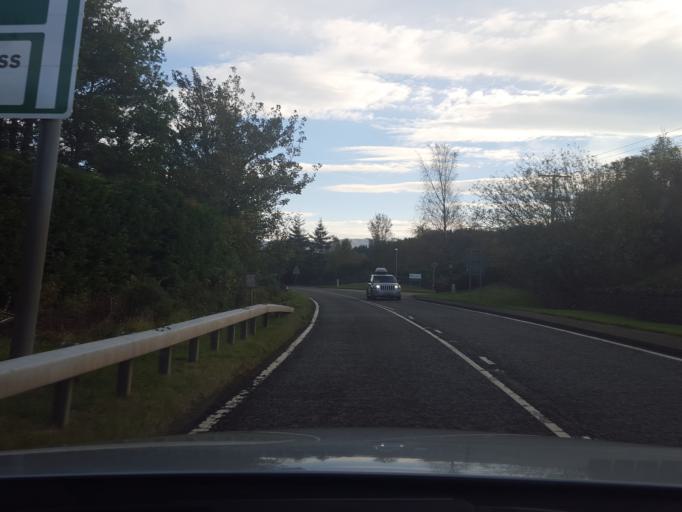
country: GB
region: Scotland
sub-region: Highland
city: Portree
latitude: 57.2855
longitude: -5.5855
